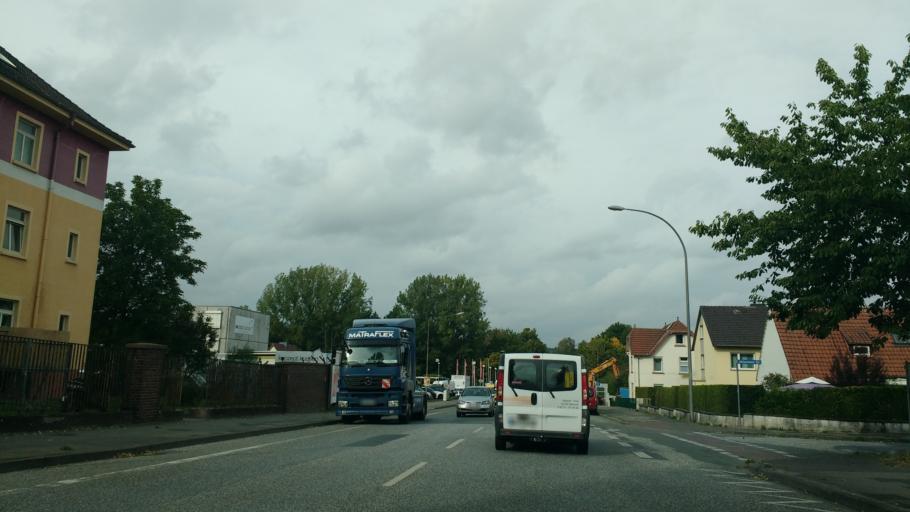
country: DE
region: North Rhine-Westphalia
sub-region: Regierungsbezirk Detmold
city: Detmold
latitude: 51.9518
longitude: 8.8797
